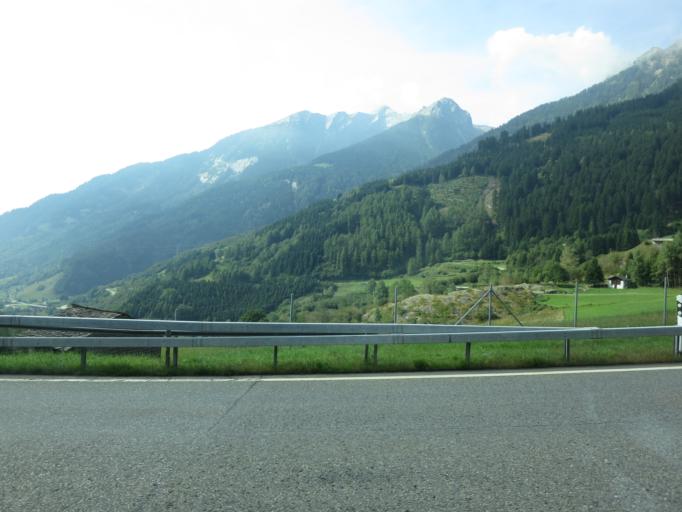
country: CH
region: Grisons
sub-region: Moesa District
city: Mesocco
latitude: 46.4127
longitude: 9.2353
